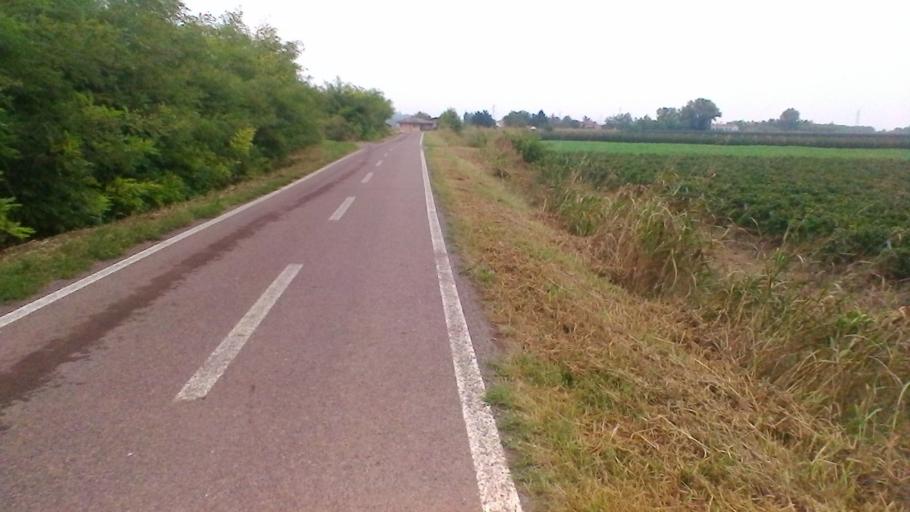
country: IT
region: Veneto
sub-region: Provincia di Verona
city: San Martino Buon Albergo
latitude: 45.3896
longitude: 11.0735
